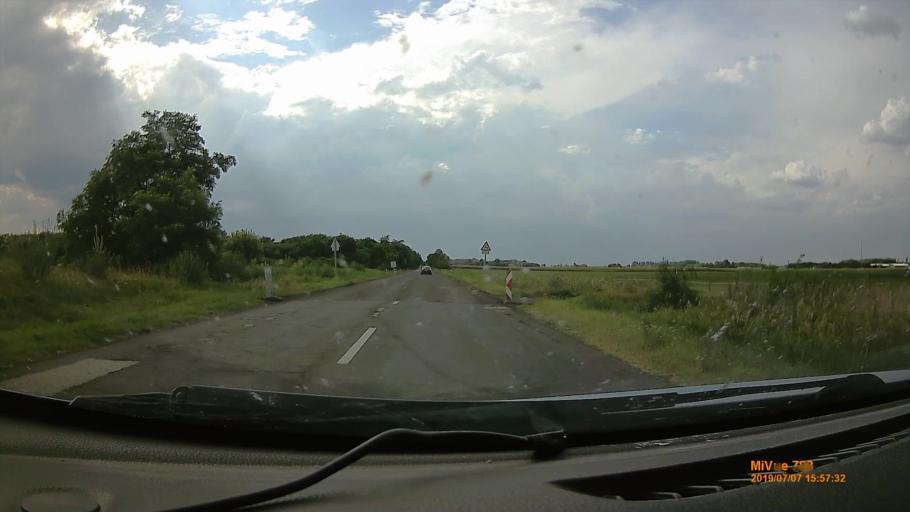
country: HU
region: Pest
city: Szentlorinckata
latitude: 47.5774
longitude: 19.7596
